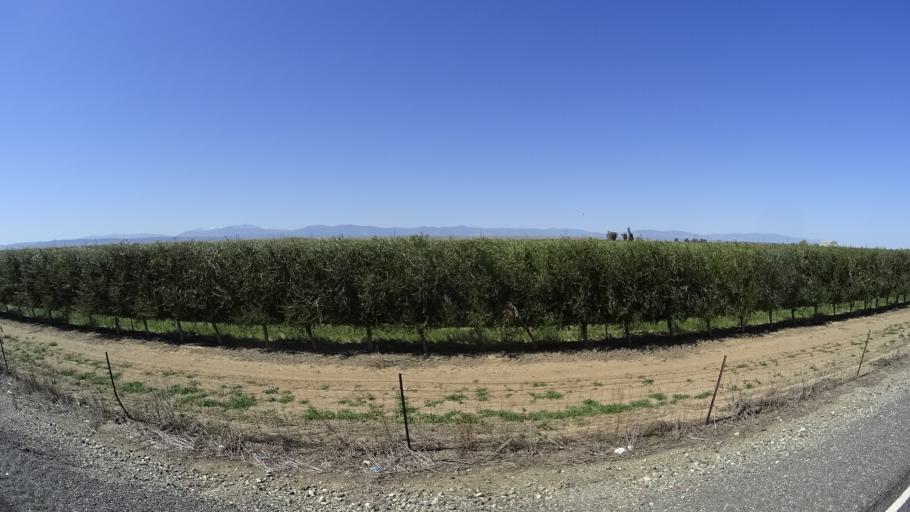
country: US
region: California
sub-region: Glenn County
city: Willows
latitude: 39.5947
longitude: -122.2498
